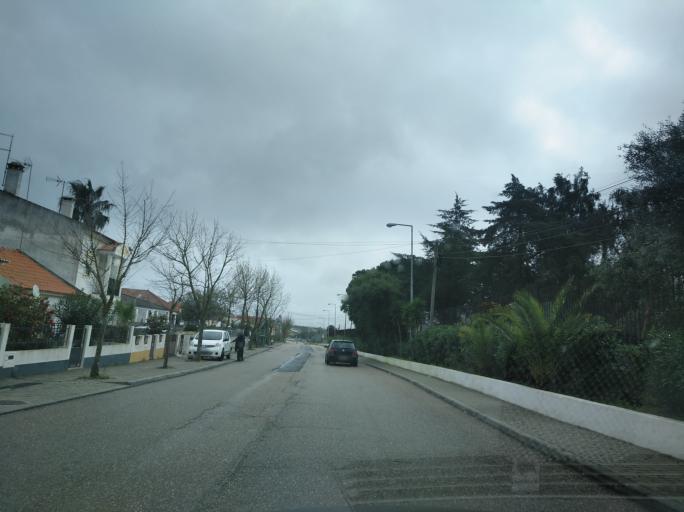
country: PT
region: Setubal
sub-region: Grandola
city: Grandola
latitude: 38.1714
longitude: -8.5581
